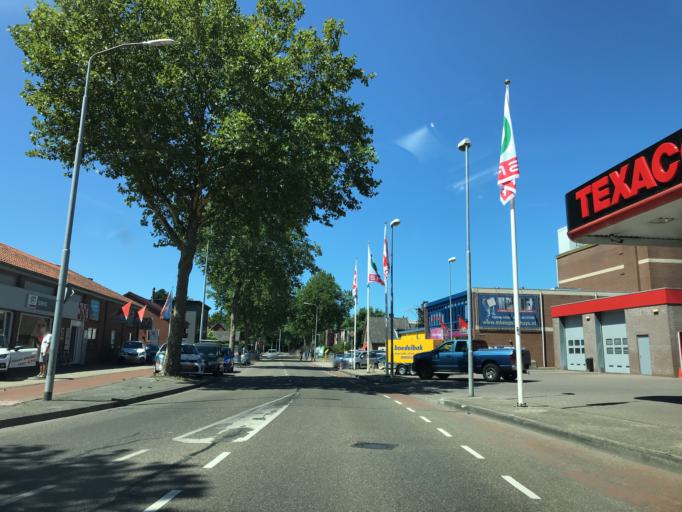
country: NL
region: North Holland
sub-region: Gemeente Huizen
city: Huizen
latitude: 52.3001
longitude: 5.2403
